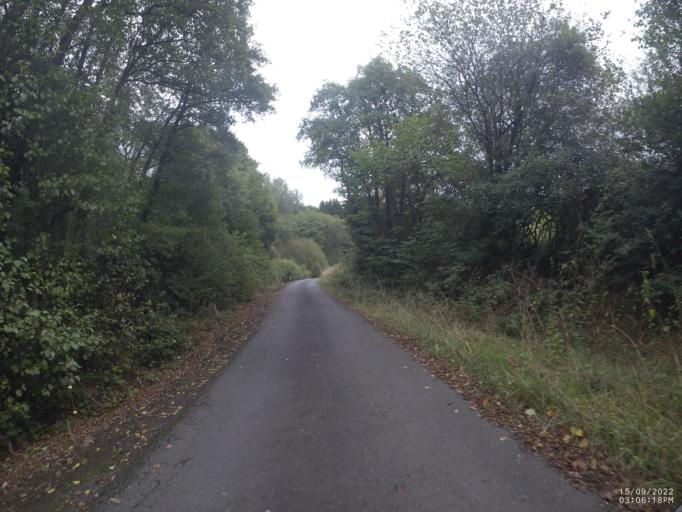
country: DE
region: Rheinland-Pfalz
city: Bongard
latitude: 50.2938
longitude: 6.8142
